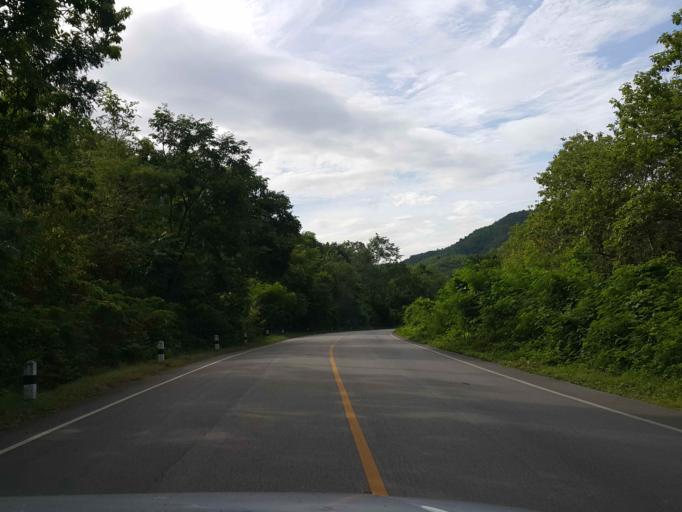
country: TH
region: Sukhothai
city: Thung Saliam
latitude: 17.3387
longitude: 99.4748
